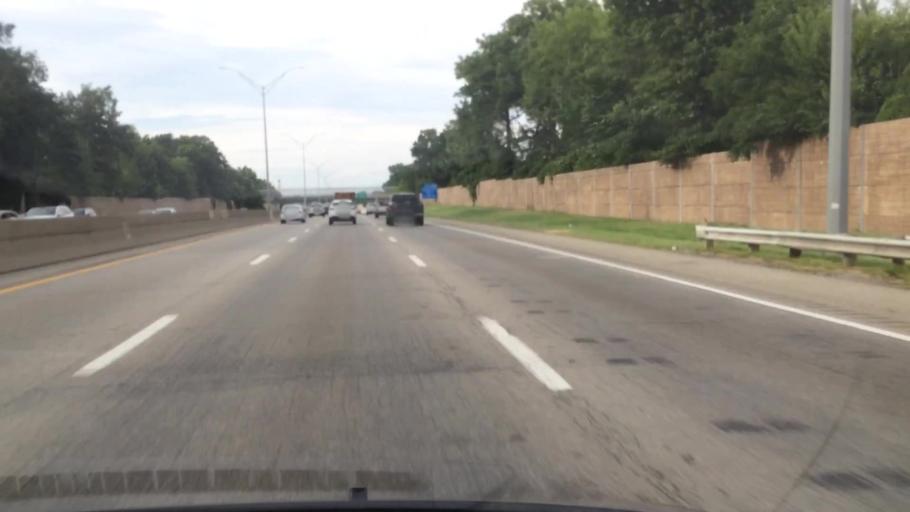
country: US
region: Ohio
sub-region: Cuyahoga County
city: Brook Park
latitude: 41.3857
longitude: -81.8174
